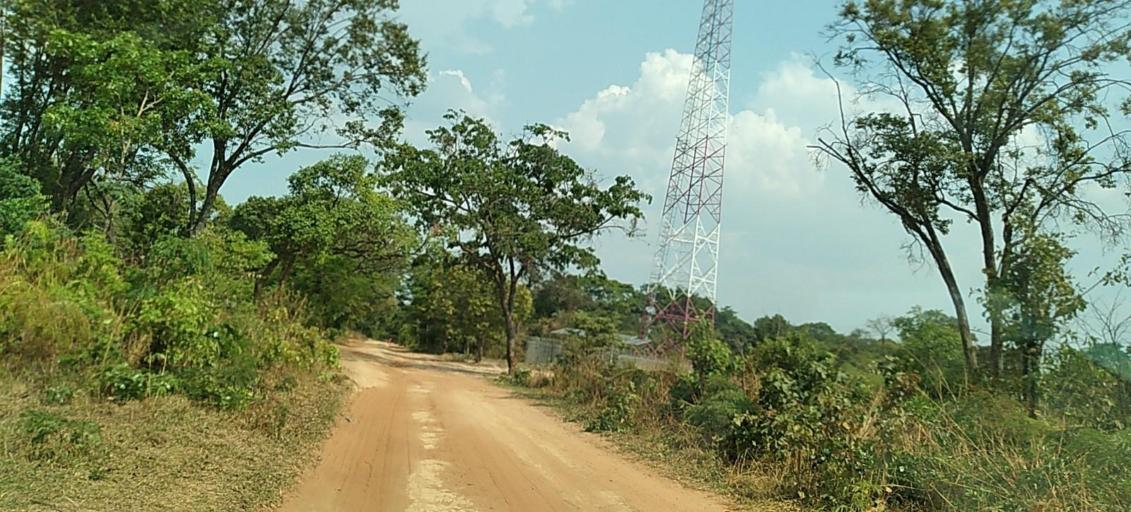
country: ZM
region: Copperbelt
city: Chingola
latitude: -12.7501
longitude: 27.7849
